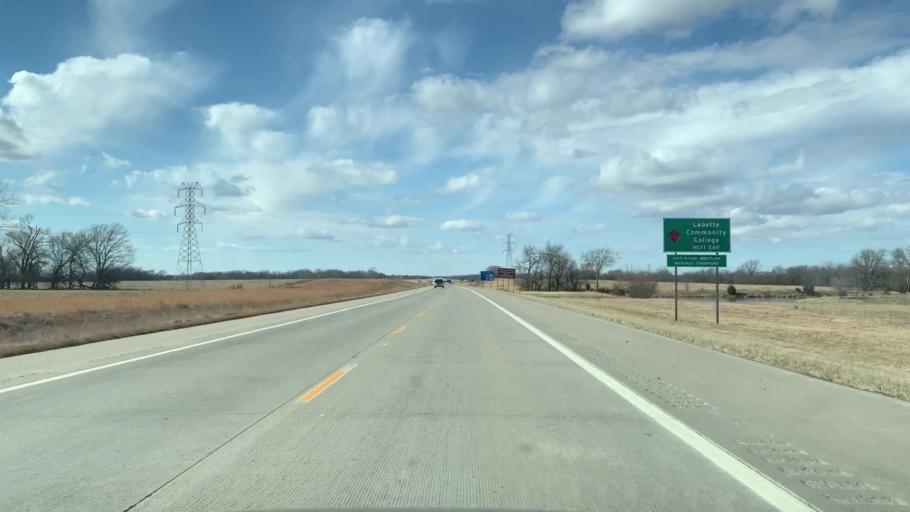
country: US
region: Kansas
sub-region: Labette County
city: Parsons
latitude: 37.3635
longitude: -95.2382
